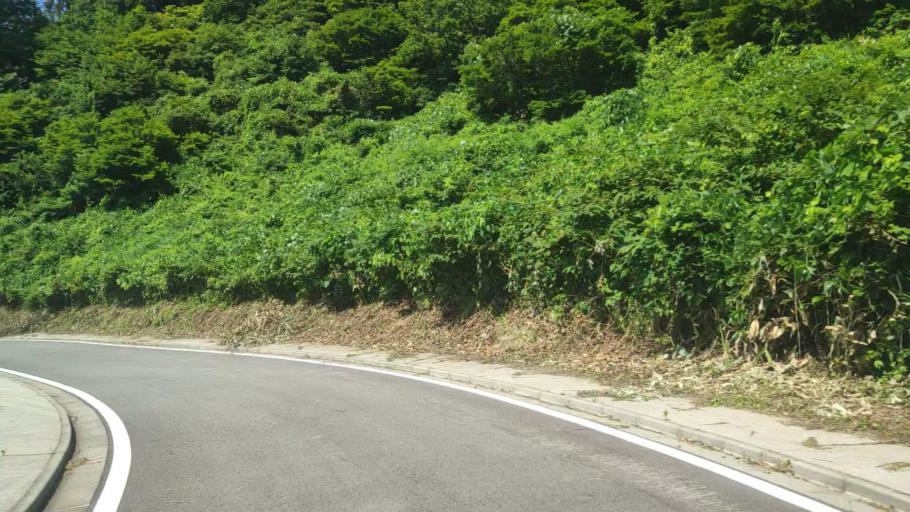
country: JP
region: Fukui
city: Katsuyama
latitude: 36.1378
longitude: 136.5146
